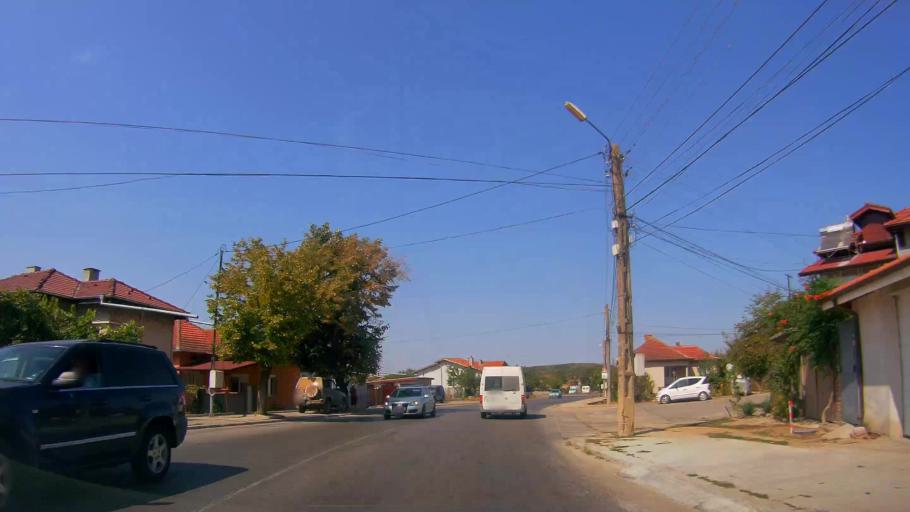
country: BG
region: Razgrad
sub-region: Obshtina Tsar Kaloyan
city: Tsar Kaloyan
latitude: 43.6015
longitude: 26.2449
